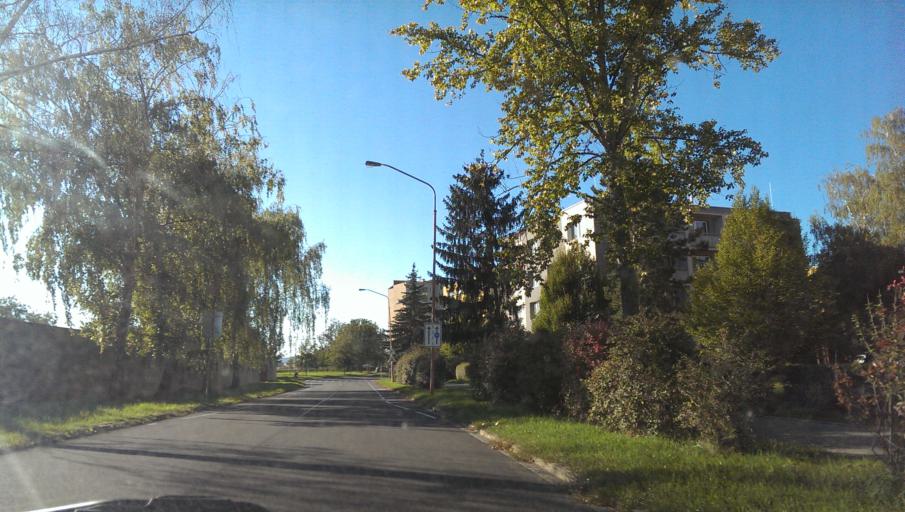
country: CZ
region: Zlin
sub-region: Okres Uherske Hradiste
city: Uherske Hradiste
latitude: 49.0704
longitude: 17.4532
